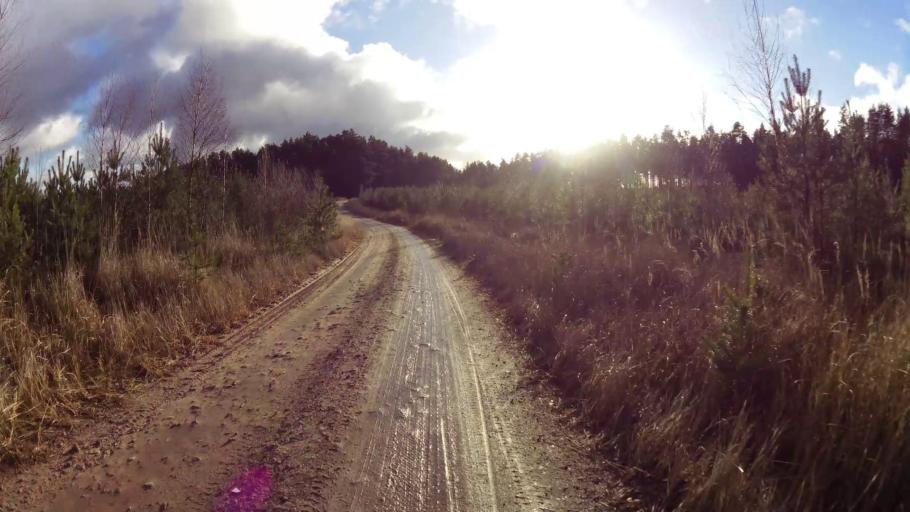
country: PL
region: West Pomeranian Voivodeship
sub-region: Powiat koszalinski
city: Sianow
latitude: 54.1077
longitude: 16.2974
